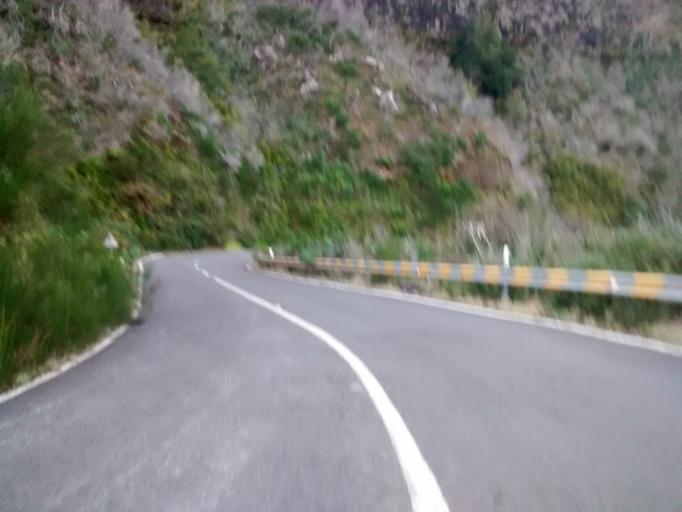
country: PT
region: Madeira
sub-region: Sao Vicente
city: Sao Vicente
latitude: 32.7440
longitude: -17.0434
